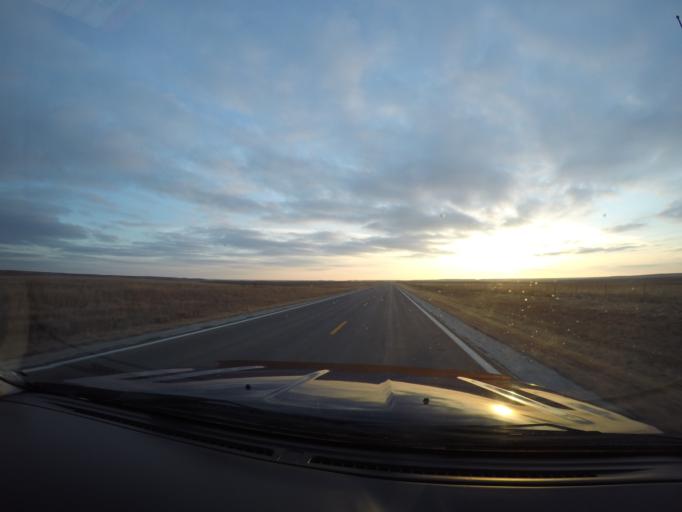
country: US
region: Kansas
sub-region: Chase County
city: Cottonwood Falls
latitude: 38.5107
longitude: -96.5452
